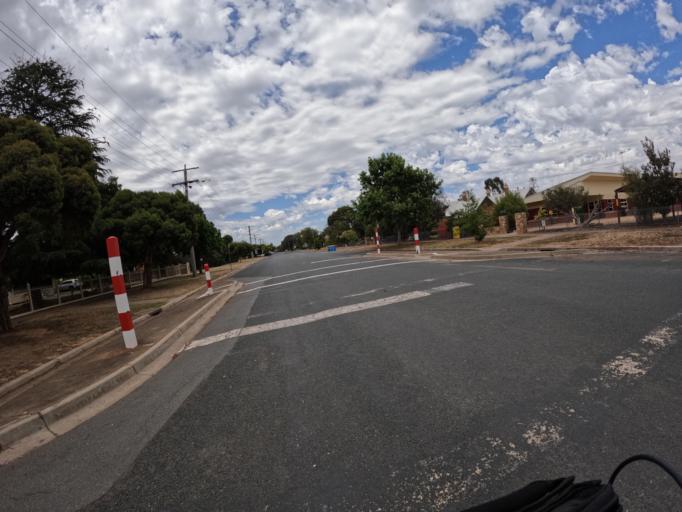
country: AU
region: Victoria
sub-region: Greater Shepparton
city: Shepparton
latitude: -36.6168
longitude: 145.2152
